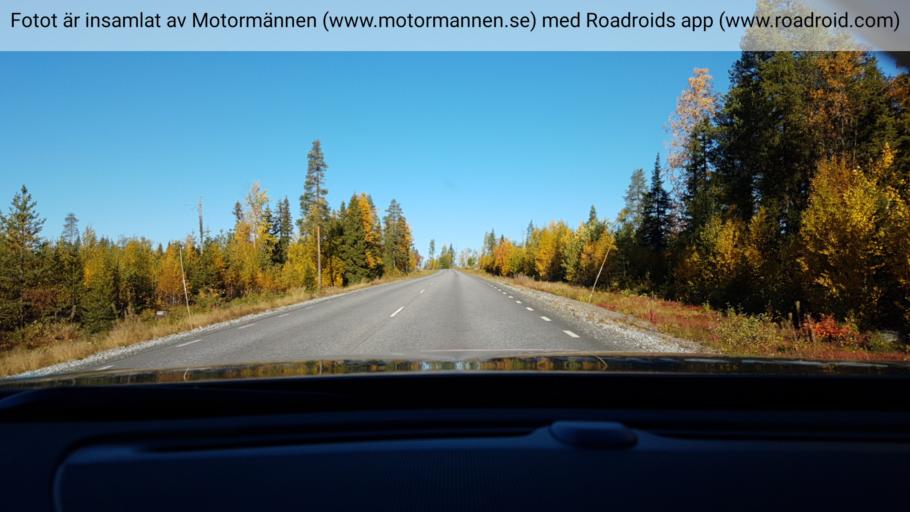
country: SE
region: Vaesterbotten
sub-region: Skelleftea Kommun
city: Storvik
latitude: 65.3482
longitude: 20.5030
